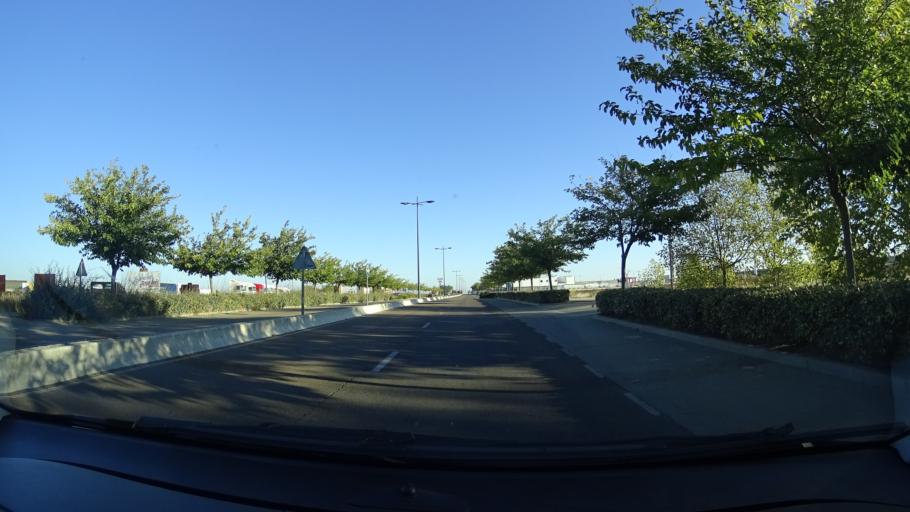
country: ES
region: Extremadura
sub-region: Provincia de Badajoz
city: Almendralejo
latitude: 38.7064
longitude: -6.4007
